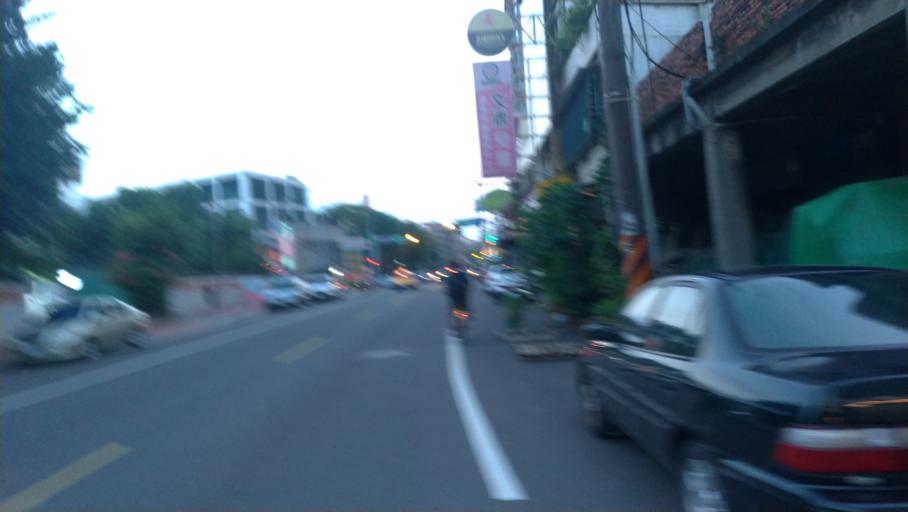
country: TW
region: Taiwan
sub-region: Taoyuan
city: Taoyuan
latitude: 24.9821
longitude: 121.3148
